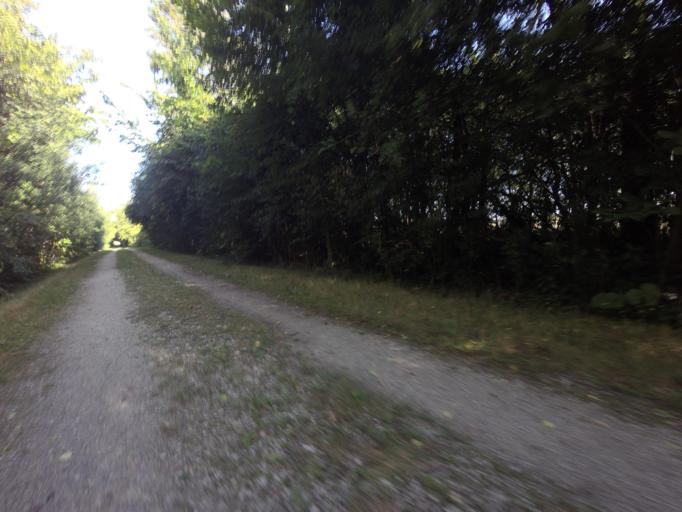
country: CA
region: Ontario
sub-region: Wellington County
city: Guelph
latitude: 43.6572
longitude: -80.4247
